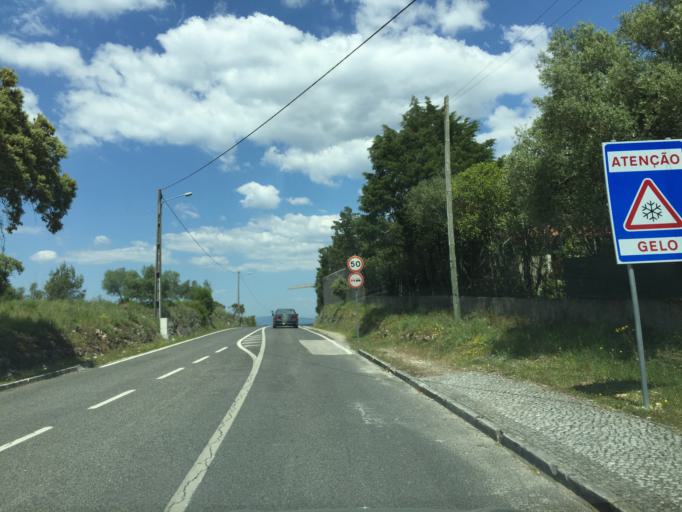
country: PT
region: Santarem
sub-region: Ourem
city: Fatima
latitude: 39.6333
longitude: -8.6643
